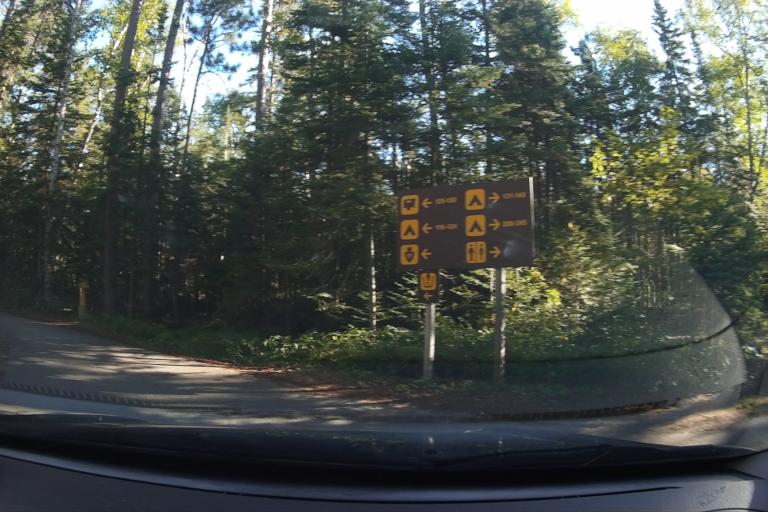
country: CA
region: Ontario
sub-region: Algoma
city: Sault Ste. Marie
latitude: 47.3293
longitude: -84.6125
